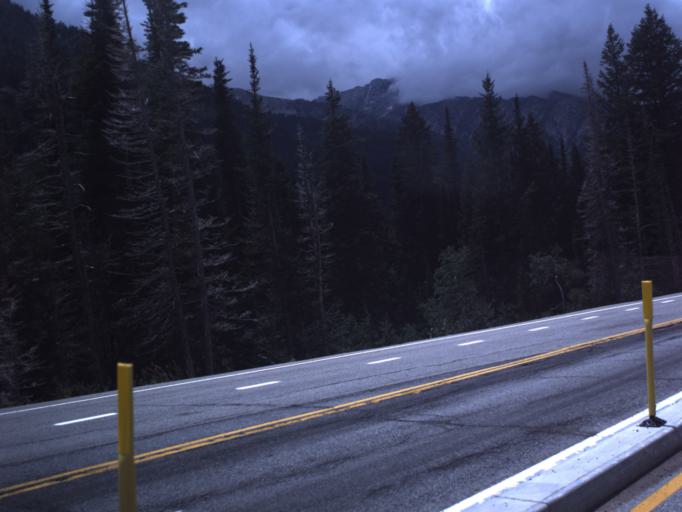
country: US
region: Utah
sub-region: Salt Lake County
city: Granite
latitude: 40.5782
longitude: -111.6711
